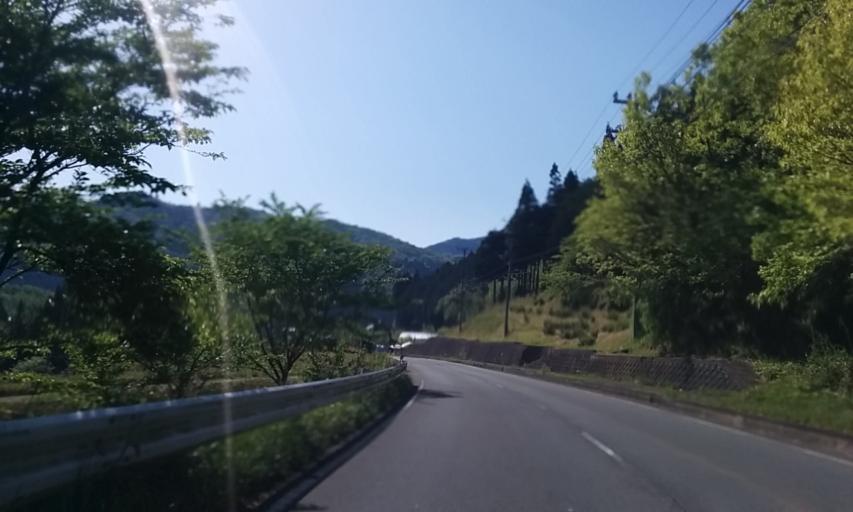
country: JP
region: Kyoto
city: Ayabe
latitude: 35.2634
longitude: 135.4400
